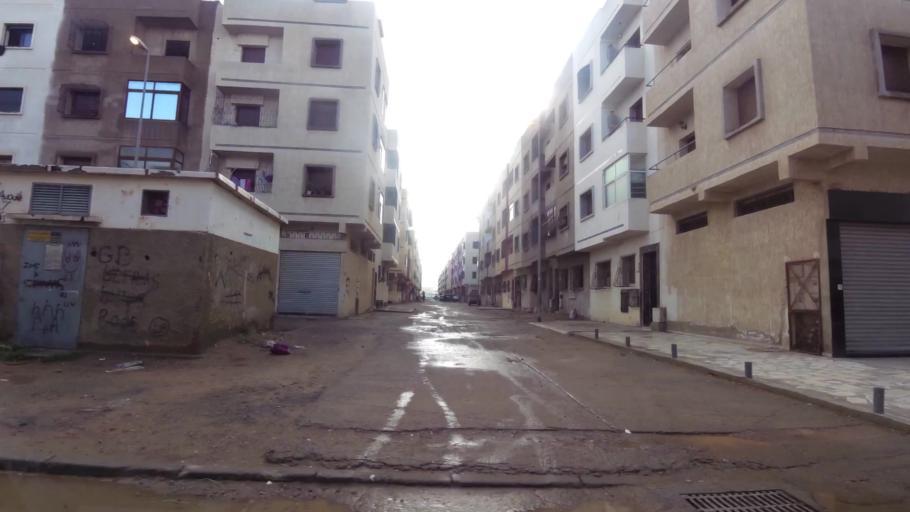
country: MA
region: Grand Casablanca
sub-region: Nouaceur
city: Bouskoura
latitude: 33.5340
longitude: -7.7047
